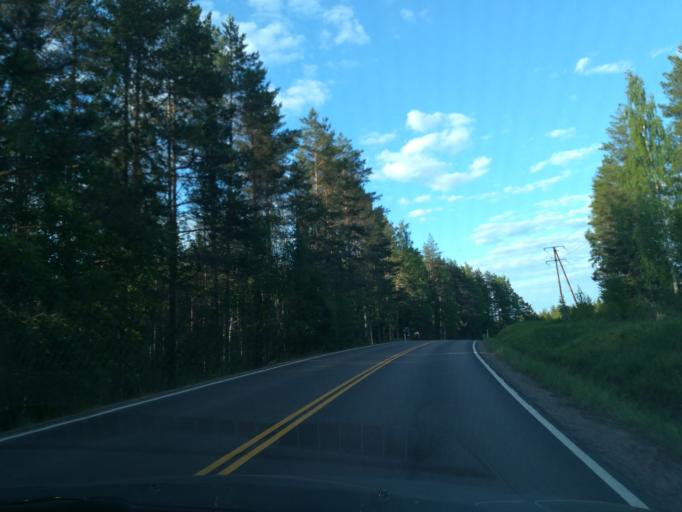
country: FI
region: Southern Savonia
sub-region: Mikkeli
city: Puumala
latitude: 61.5778
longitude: 28.1616
